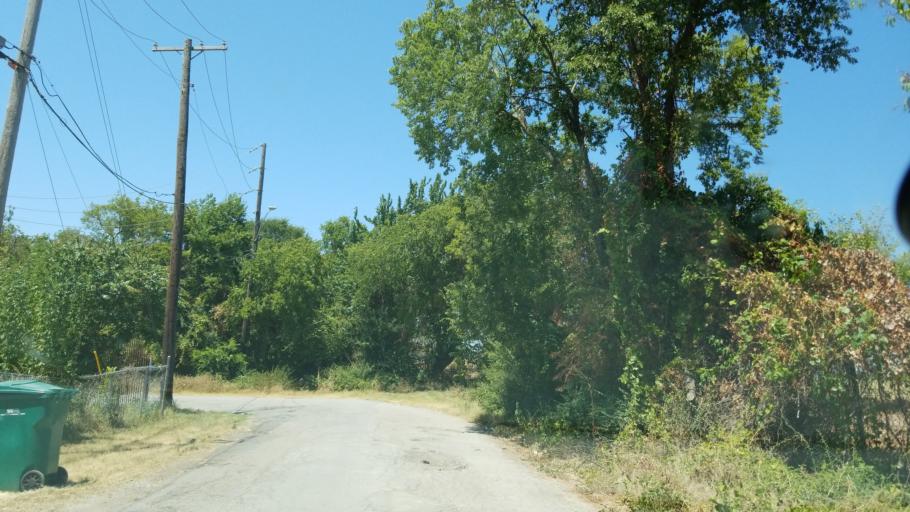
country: US
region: Texas
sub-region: Dallas County
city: Cockrell Hill
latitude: 32.7449
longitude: -96.8937
